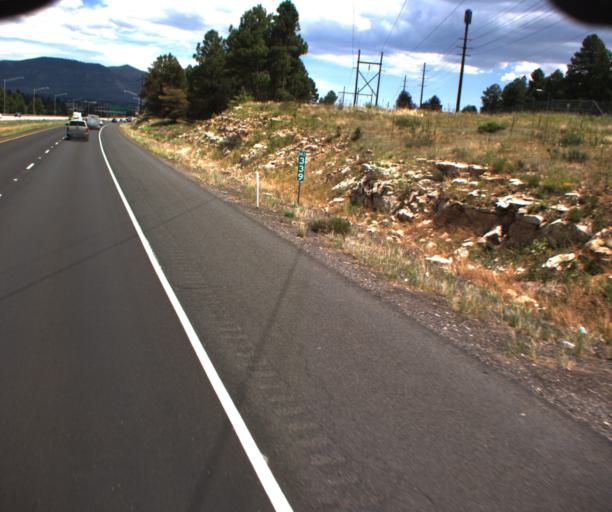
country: US
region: Arizona
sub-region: Coconino County
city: Flagstaff
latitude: 35.1613
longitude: -111.6753
